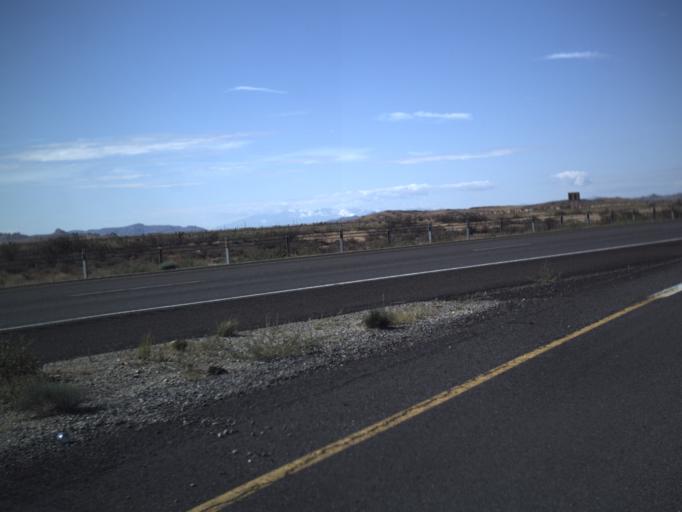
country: US
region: Utah
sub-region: Tooele County
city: Grantsville
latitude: 40.7312
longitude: -113.1190
